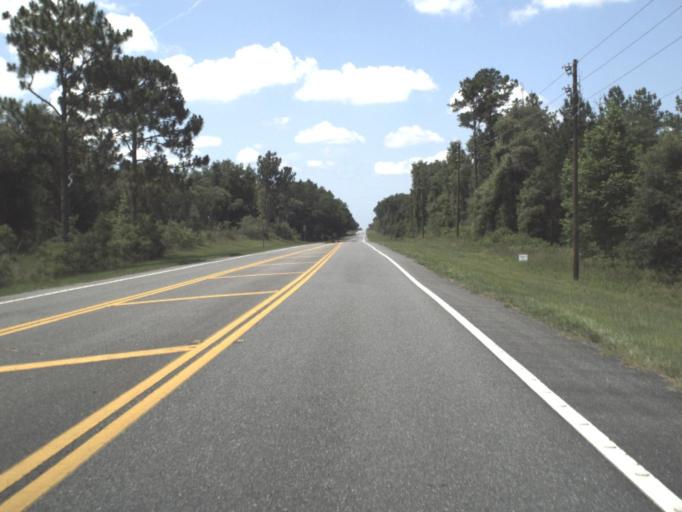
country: US
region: Florida
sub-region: Levy County
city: Williston Highlands
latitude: 29.2885
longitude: -82.5360
